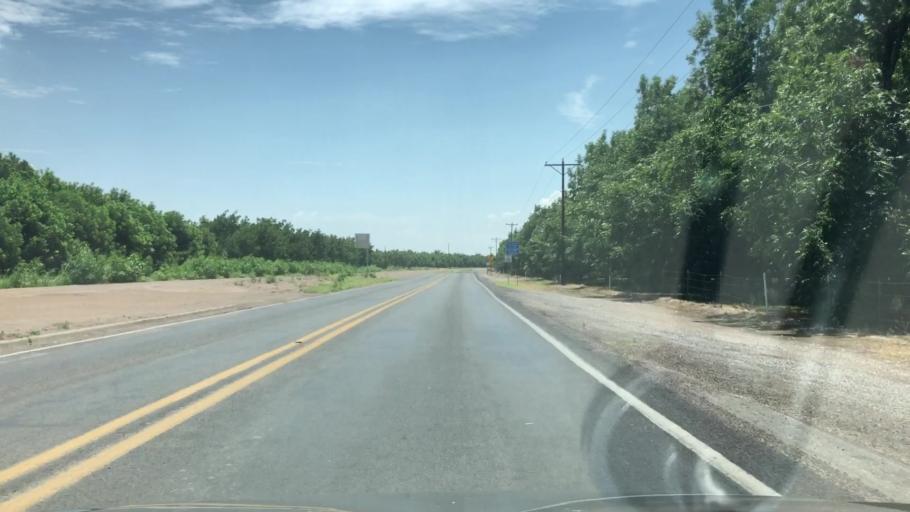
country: US
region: New Mexico
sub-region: Dona Ana County
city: La Union
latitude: 31.9951
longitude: -106.6538
